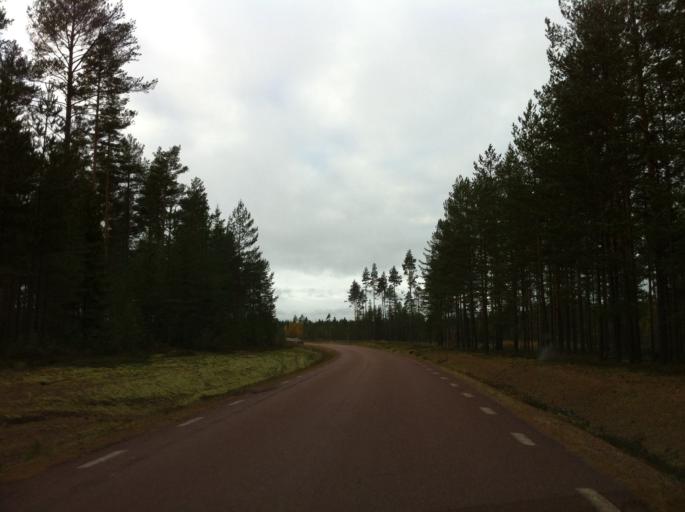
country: SE
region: Dalarna
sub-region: Mora Kommun
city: Mora
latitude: 61.1036
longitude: 14.4510
